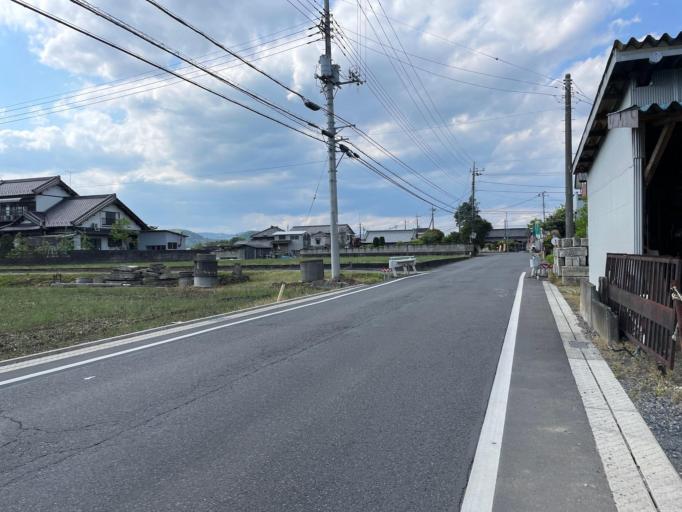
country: JP
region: Tochigi
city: Tochigi
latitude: 36.4099
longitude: 139.7353
